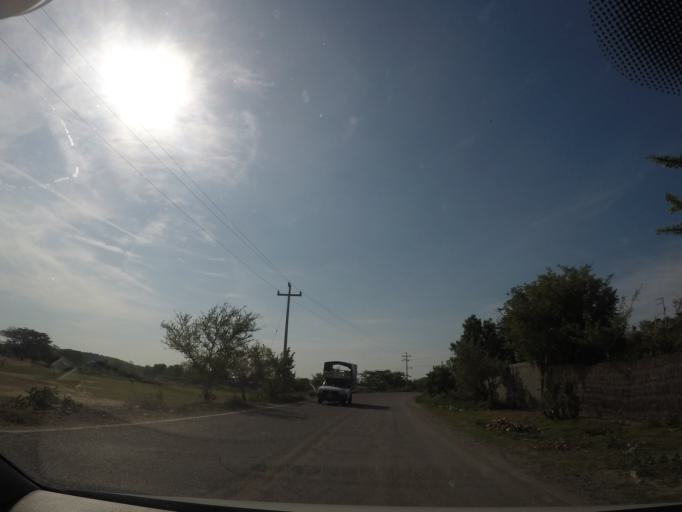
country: MX
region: Oaxaca
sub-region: Salina Cruz
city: Salina Cruz
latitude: 16.2208
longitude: -95.1264
